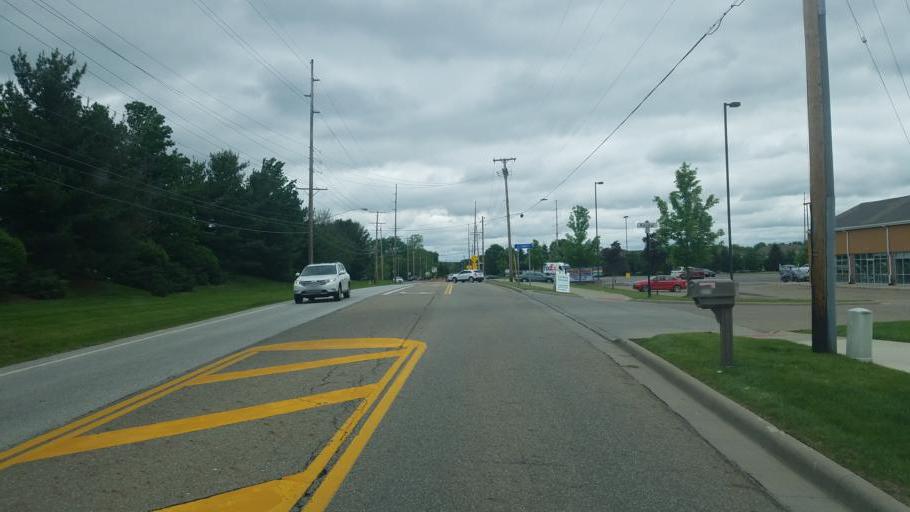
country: US
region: Ohio
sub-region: Summit County
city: Reminderville
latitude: 41.3399
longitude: -81.4189
